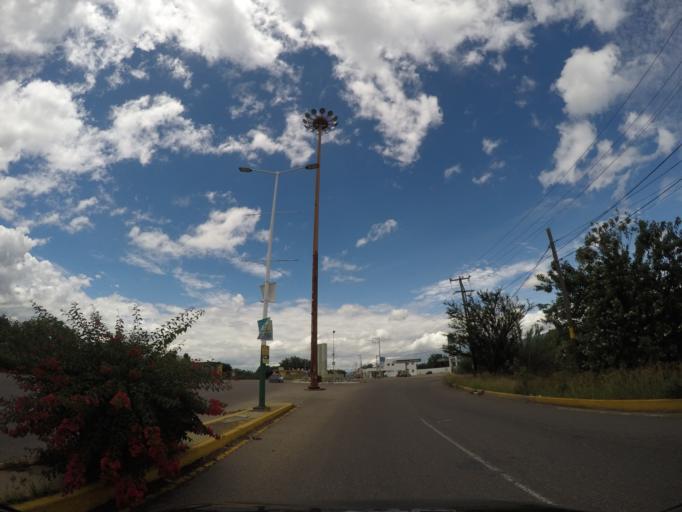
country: MX
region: Oaxaca
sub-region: Santa Cruz Xoxocotlan
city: San Isidro Monjas
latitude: 16.9972
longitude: -96.7416
